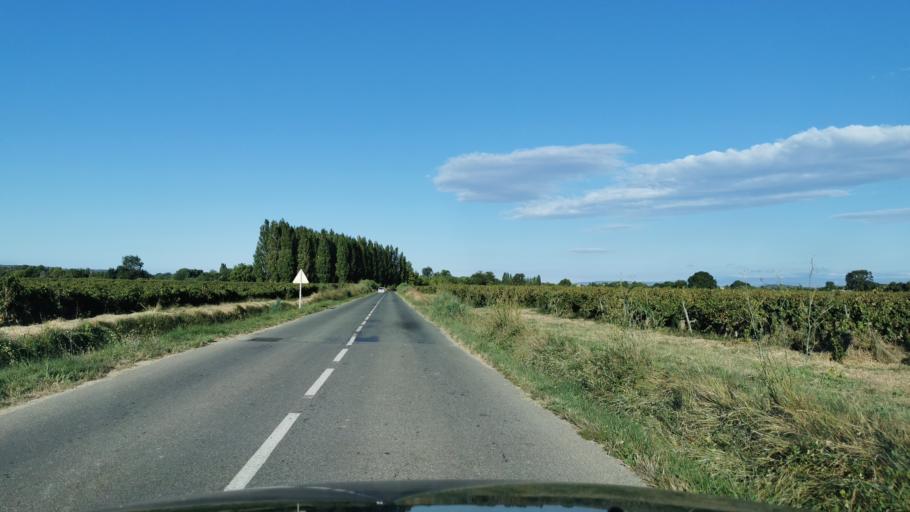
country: FR
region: Languedoc-Roussillon
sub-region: Departement de l'Aude
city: Coursan
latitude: 43.2457
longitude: 3.0159
